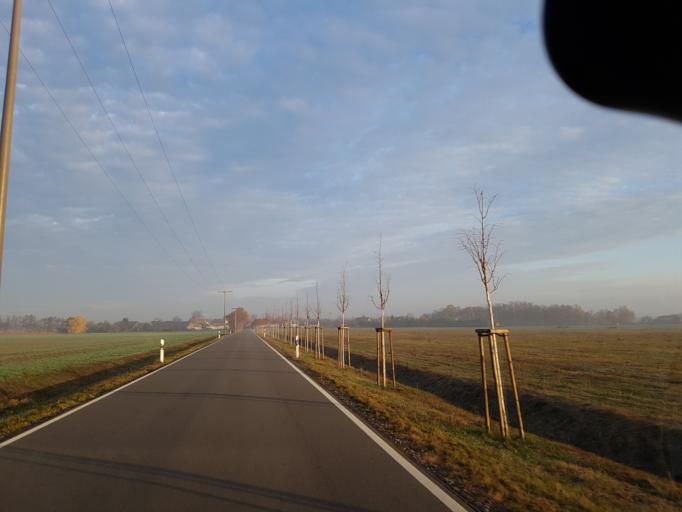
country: DE
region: Saxony-Anhalt
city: Elster
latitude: 51.8598
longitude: 12.8452
